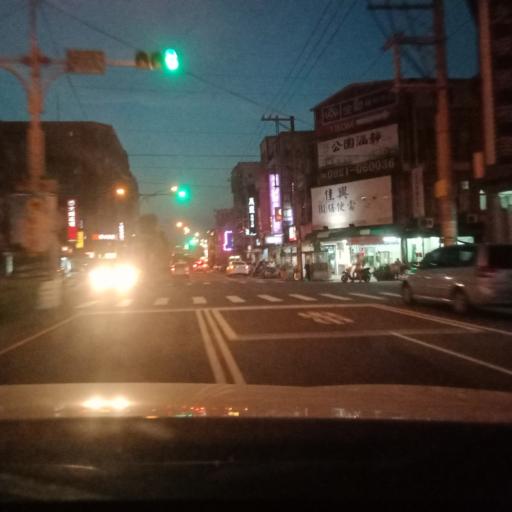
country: TW
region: Taiwan
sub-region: Hsinchu
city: Zhubei
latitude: 24.9030
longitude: 121.0468
